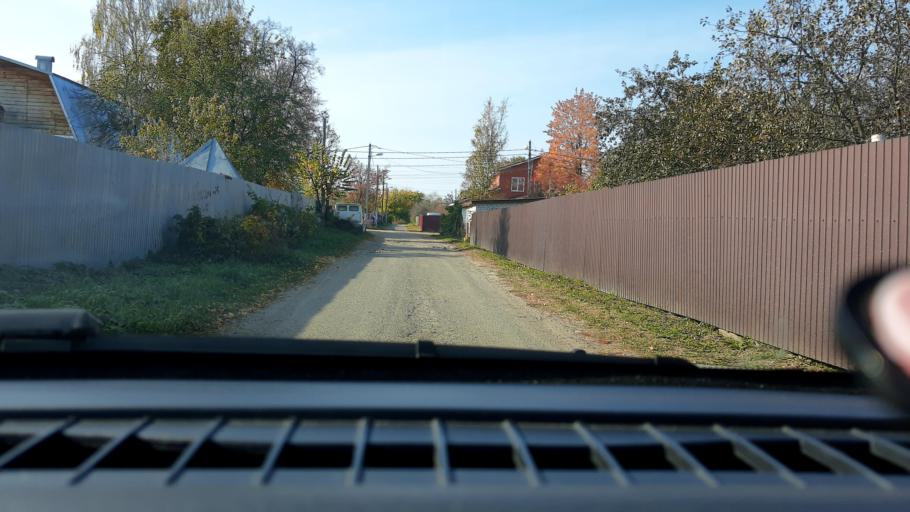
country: RU
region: Nizjnij Novgorod
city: Gorbatovka
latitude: 56.2124
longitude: 43.7556
